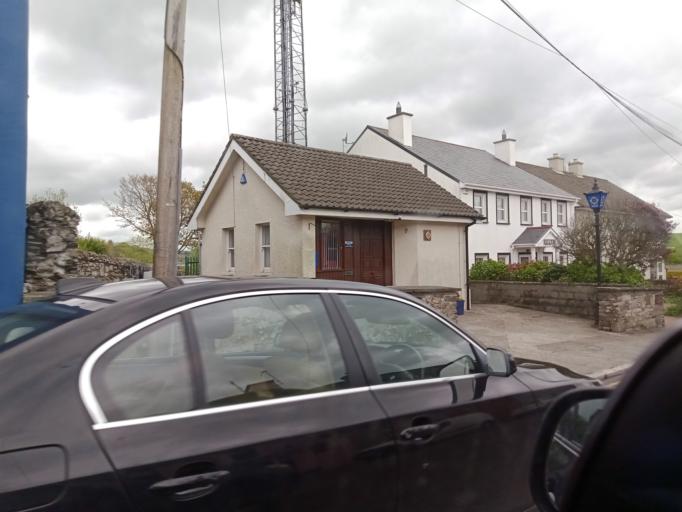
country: IE
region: Munster
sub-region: County Cork
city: Derry
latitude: 51.5775
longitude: -9.0317
